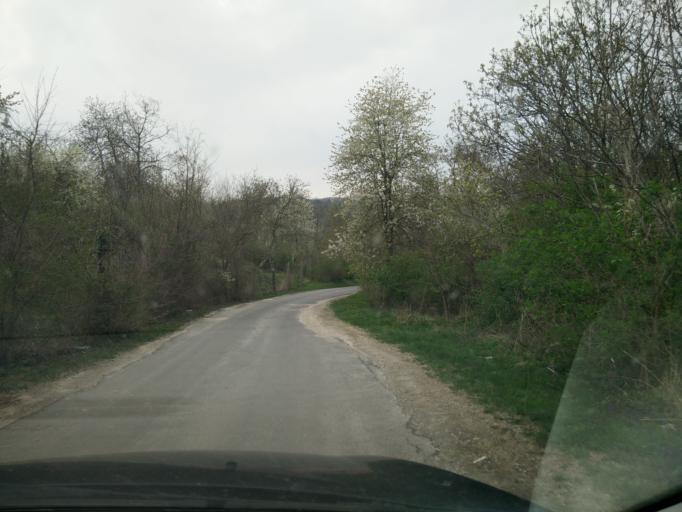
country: HU
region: Pest
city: Budaors
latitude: 47.4658
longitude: 18.9369
